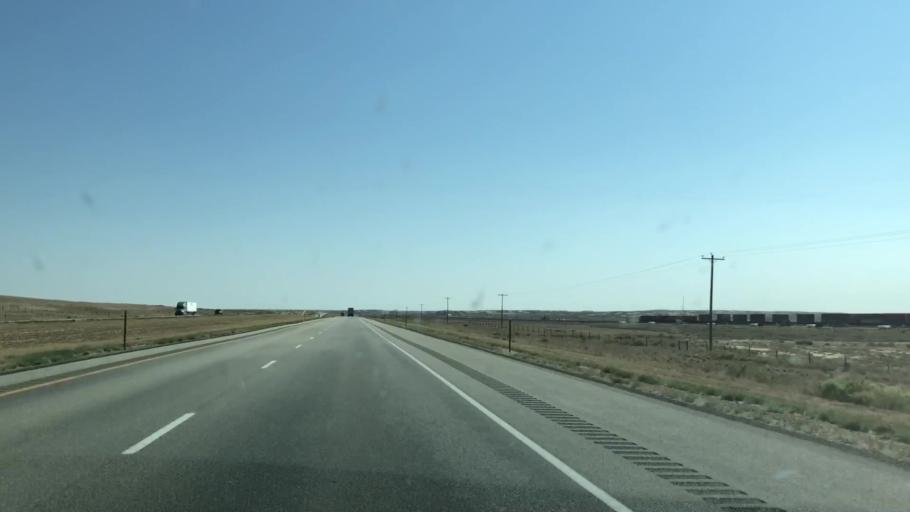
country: US
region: Wyoming
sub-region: Carbon County
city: Rawlins
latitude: 41.6924
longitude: -107.9362
